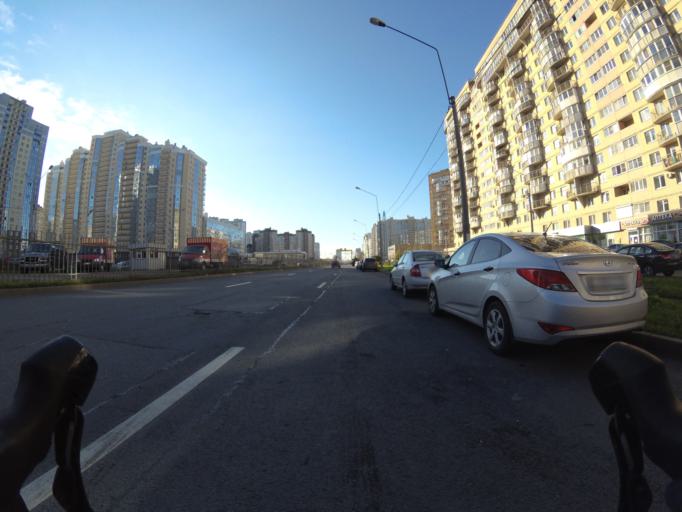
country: RU
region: Leningrad
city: Untolovo
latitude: 60.0037
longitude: 30.2106
